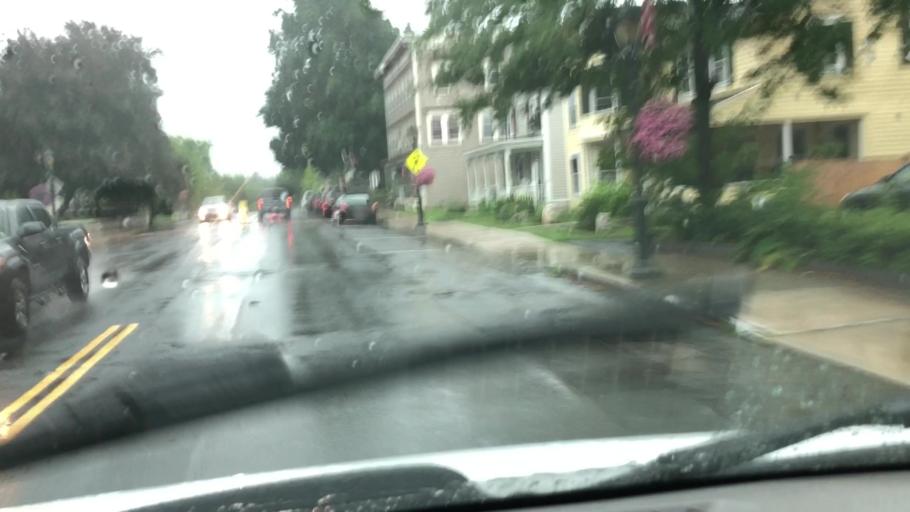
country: US
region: Massachusetts
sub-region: Berkshire County
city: Lee
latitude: 42.3074
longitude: -73.2505
